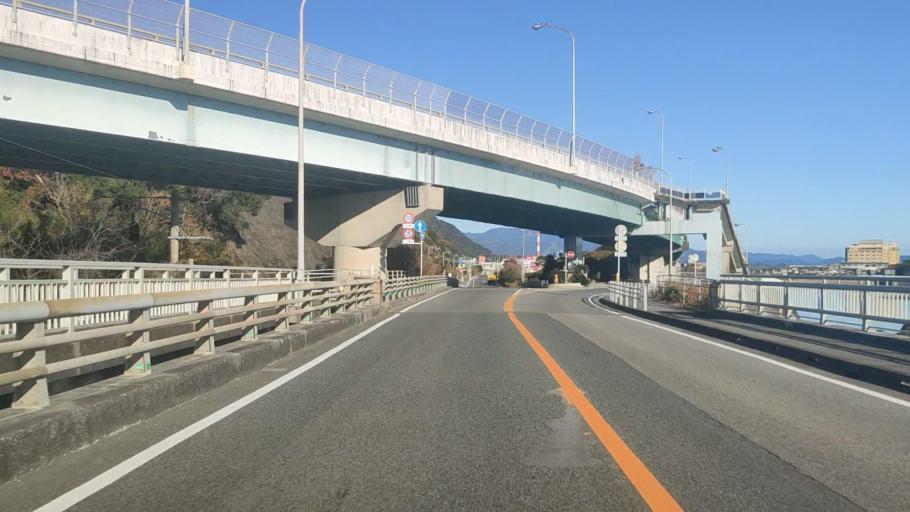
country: JP
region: Miyazaki
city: Nobeoka
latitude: 32.5368
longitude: 131.6794
